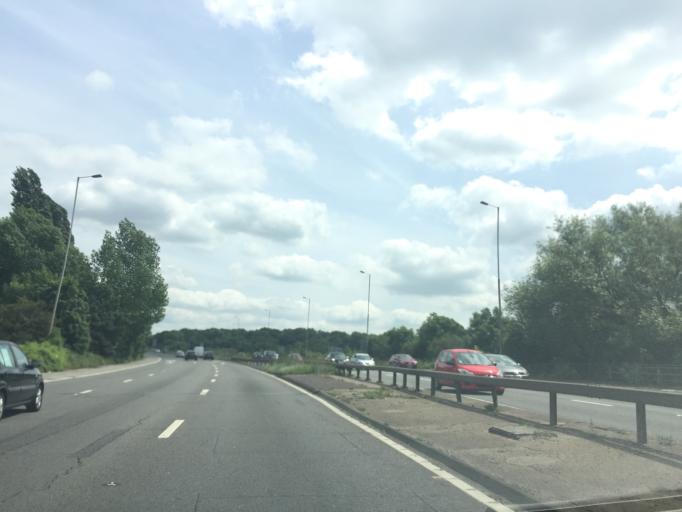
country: GB
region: England
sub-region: Greater London
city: Bexley
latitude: 51.4459
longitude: 0.1577
